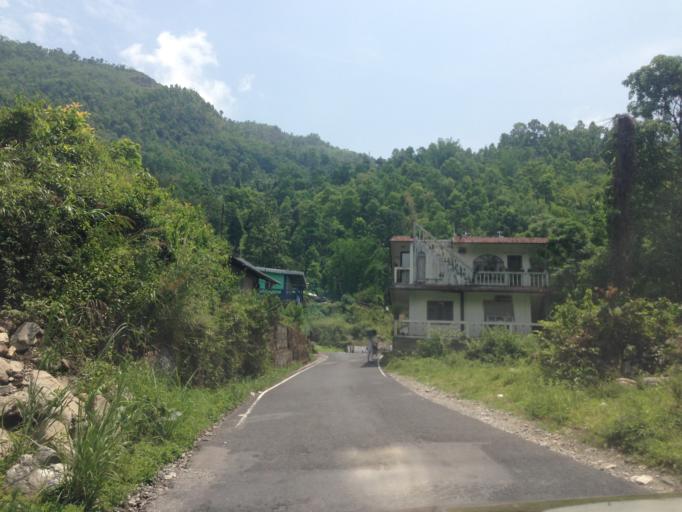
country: IN
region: West Bengal
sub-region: Darjiling
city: Karsiyang
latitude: 26.8536
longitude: 88.3008
